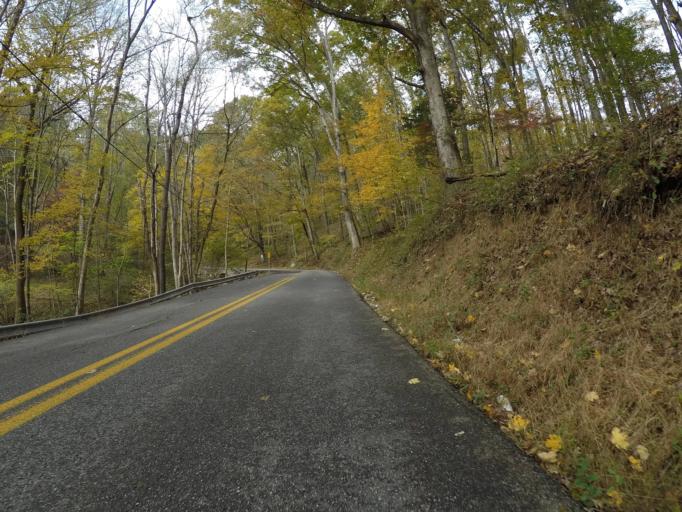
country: US
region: West Virginia
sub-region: Wayne County
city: Lavalette
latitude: 38.3680
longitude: -82.4182
